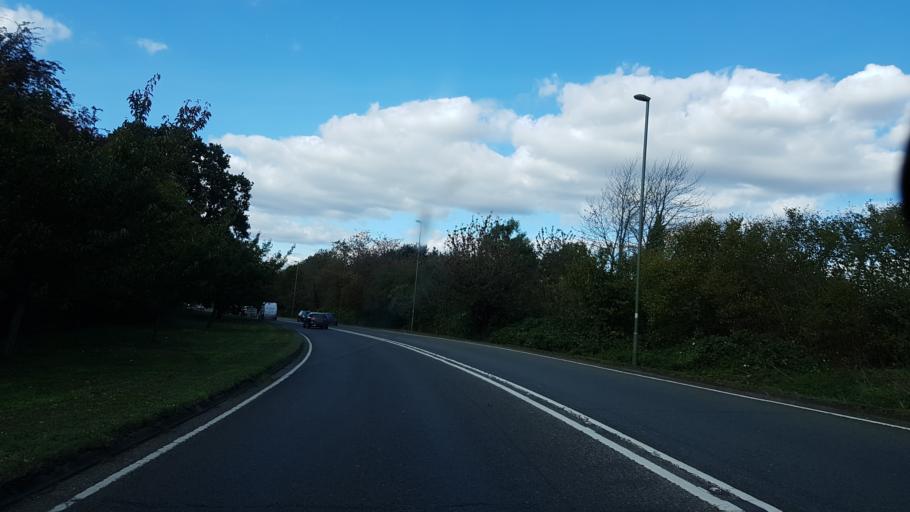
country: GB
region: England
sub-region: Surrey
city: Milford
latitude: 51.1759
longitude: -0.6487
